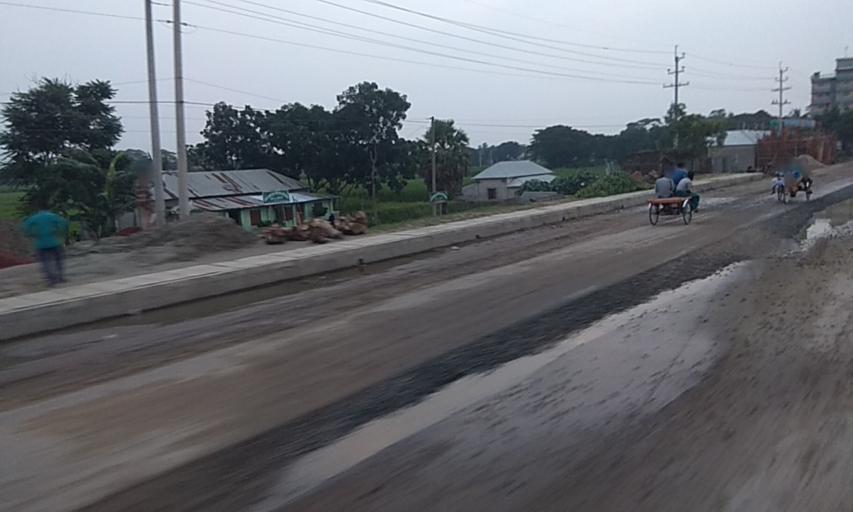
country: BD
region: Dhaka
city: Char Bhadrasan
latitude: 23.3731
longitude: 90.0291
